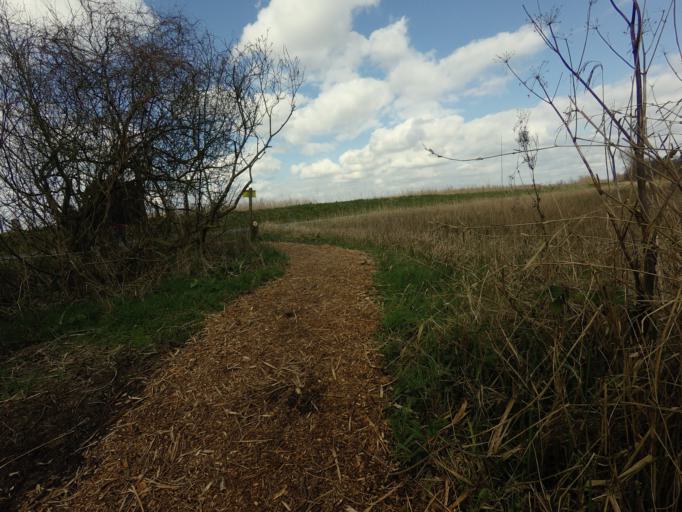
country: NL
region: Utrecht
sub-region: Gemeente De Ronde Venen
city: Mijdrecht
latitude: 52.1507
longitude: 4.8399
